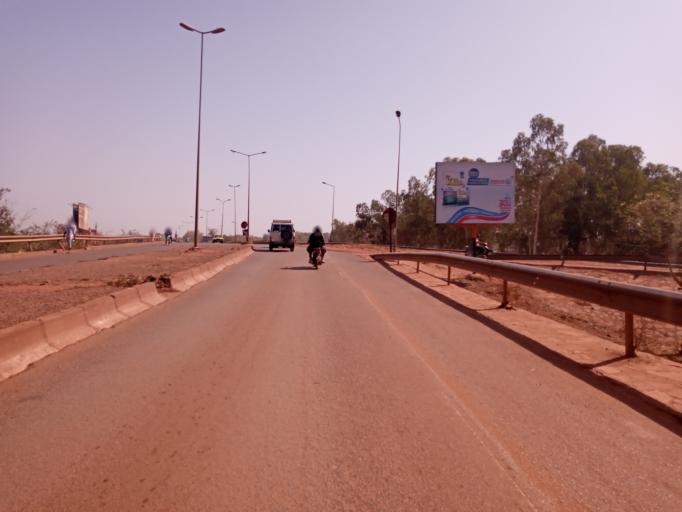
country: ML
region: Bamako
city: Bamako
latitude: 12.6080
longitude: -7.9979
